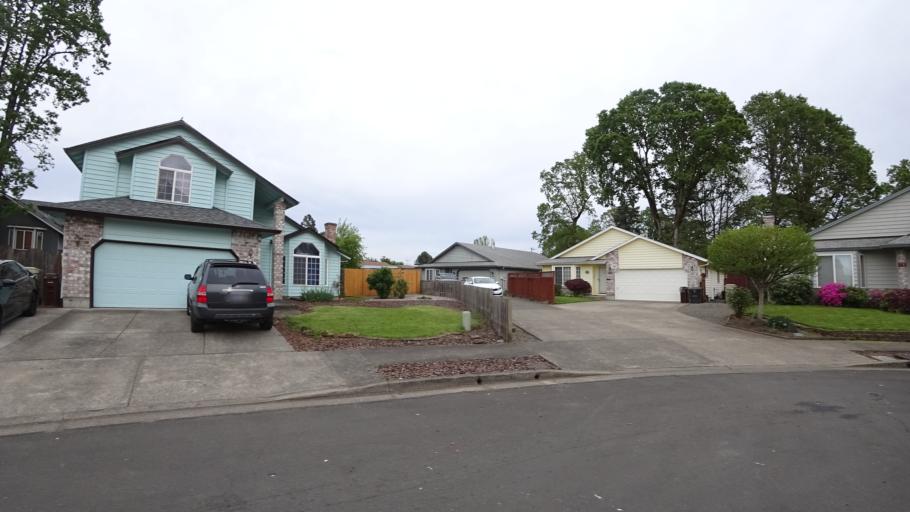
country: US
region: Oregon
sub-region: Washington County
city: Aloha
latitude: 45.5131
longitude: -122.9102
